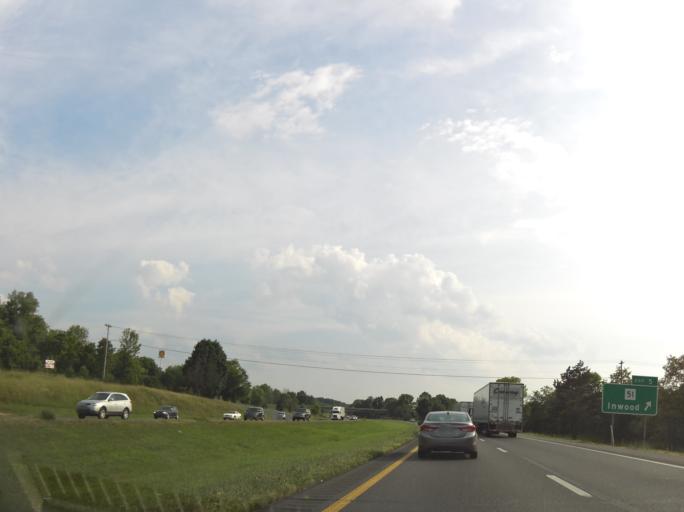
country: US
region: West Virginia
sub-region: Berkeley County
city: Inwood
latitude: 39.3662
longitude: -78.0465
